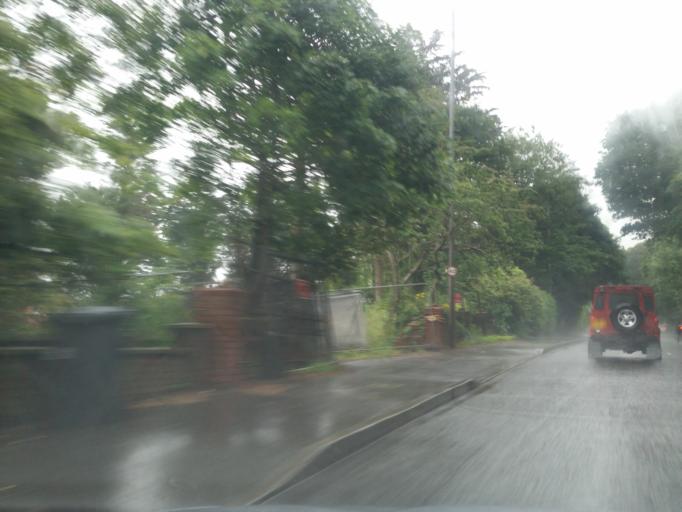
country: GB
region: Northern Ireland
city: Holywood
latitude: 54.6449
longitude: -5.8212
